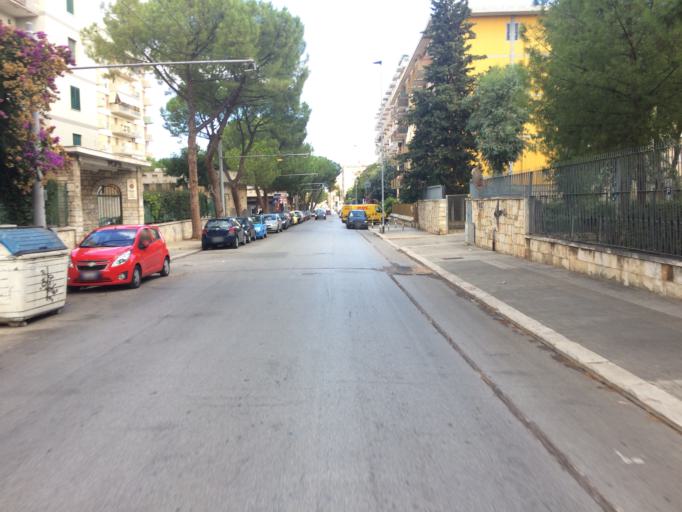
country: IT
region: Apulia
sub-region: Provincia di Bari
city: Bari
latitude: 41.1013
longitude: 16.8715
